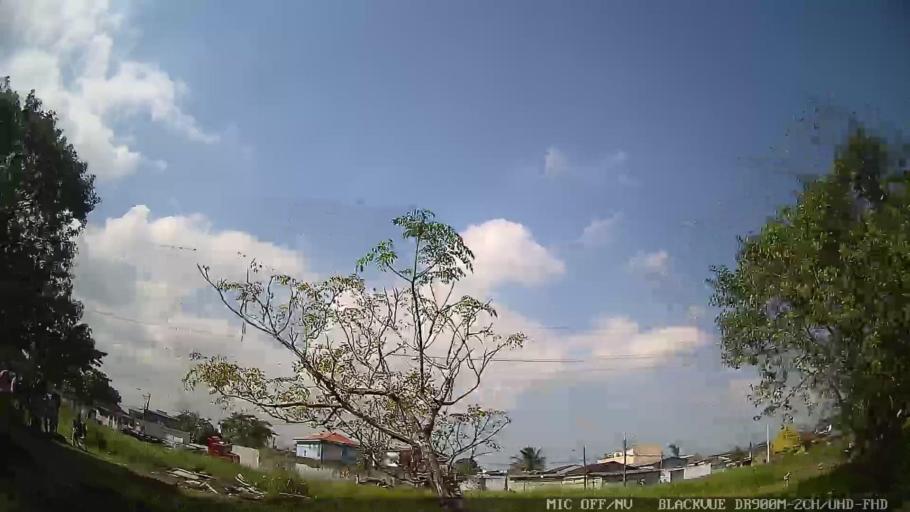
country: BR
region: Sao Paulo
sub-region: Santos
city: Santos
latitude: -23.9397
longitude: -46.2976
